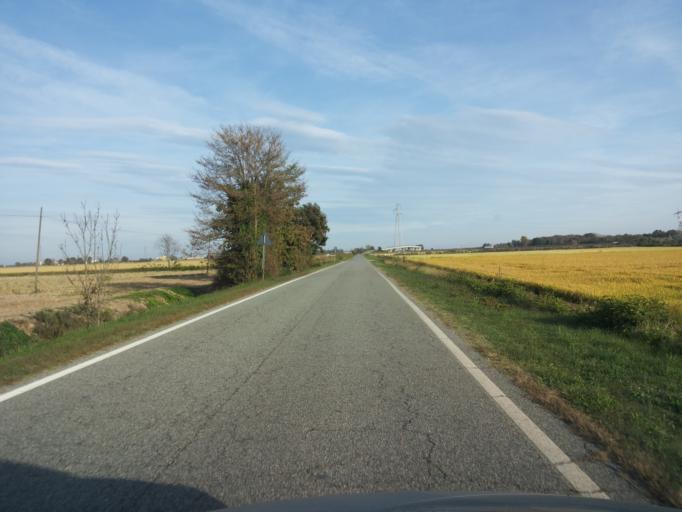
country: IT
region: Piedmont
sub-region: Provincia di Vercelli
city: Carisio
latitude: 45.4308
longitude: 8.1824
